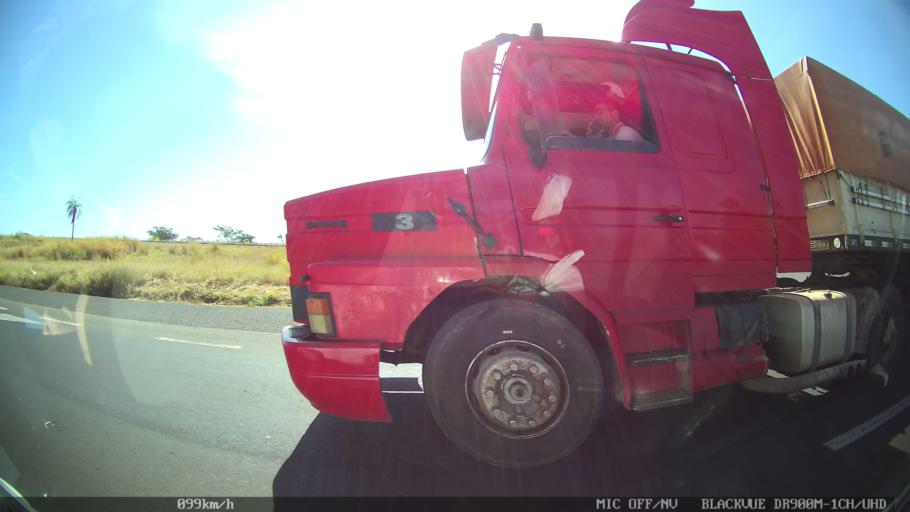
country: BR
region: Sao Paulo
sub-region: Barretos
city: Barretos
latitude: -20.6091
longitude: -48.7485
